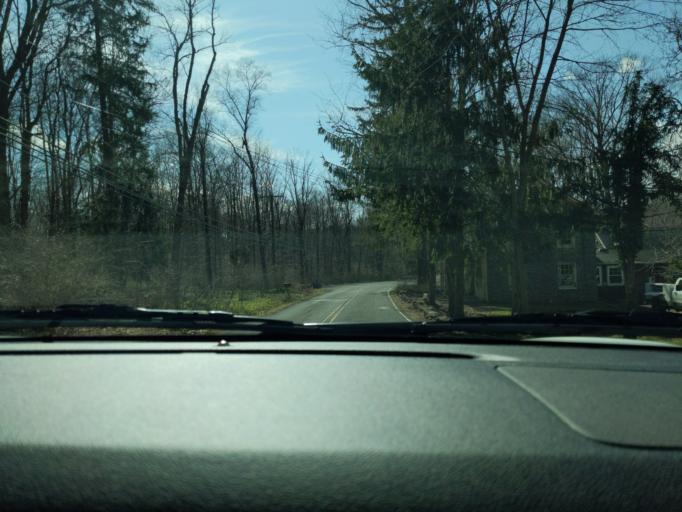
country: US
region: Pennsylvania
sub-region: Bucks County
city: Richlandtown
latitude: 40.4594
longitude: -75.2740
